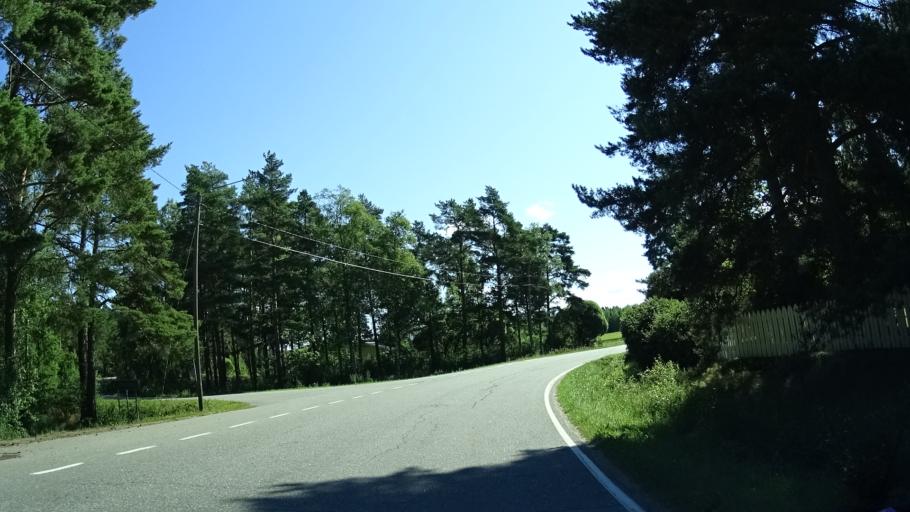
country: FI
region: Varsinais-Suomi
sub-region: Turku
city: Velkua
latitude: 60.5119
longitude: 21.7469
